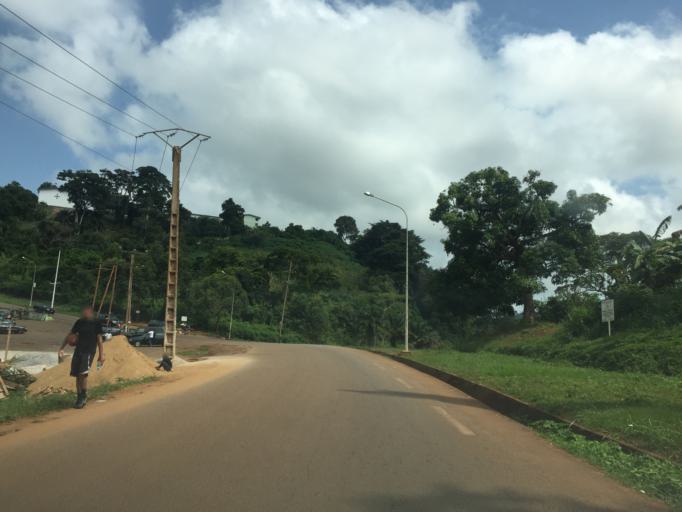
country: CM
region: Centre
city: Yaounde
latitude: 3.9144
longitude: 11.5015
